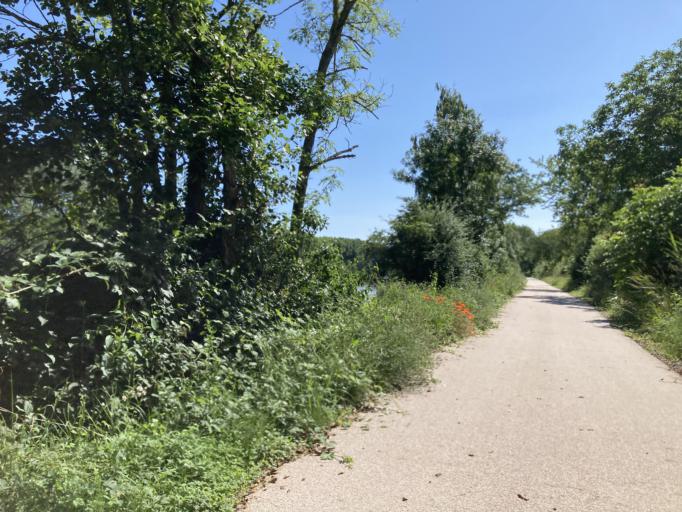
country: FR
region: Bourgogne
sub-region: Departement de l'Yonne
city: Joigny
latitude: 47.9679
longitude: 3.4372
